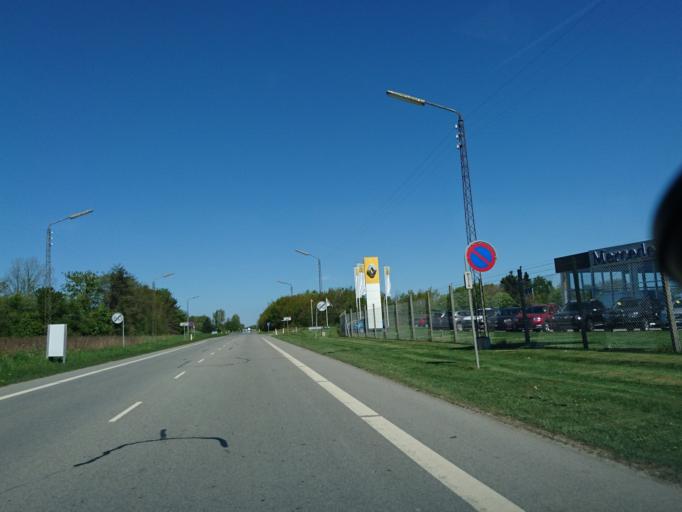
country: DK
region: North Denmark
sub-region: Hjorring Kommune
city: Hjorring
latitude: 57.4607
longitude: 10.0175
